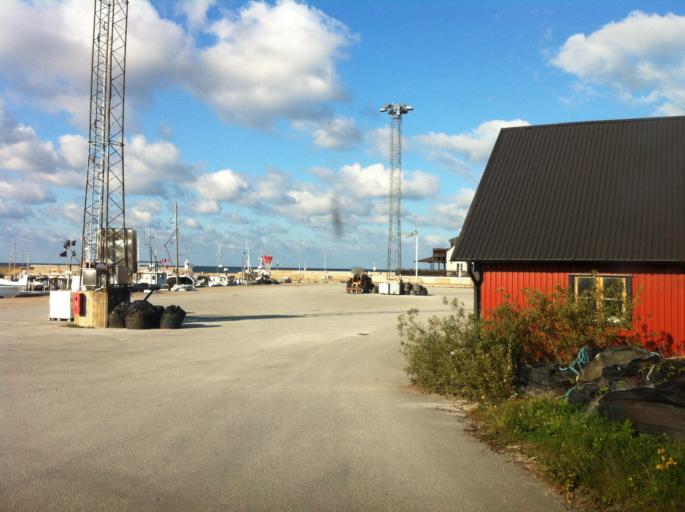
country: SE
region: Gotland
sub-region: Gotland
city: Slite
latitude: 57.4213
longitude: 18.9120
